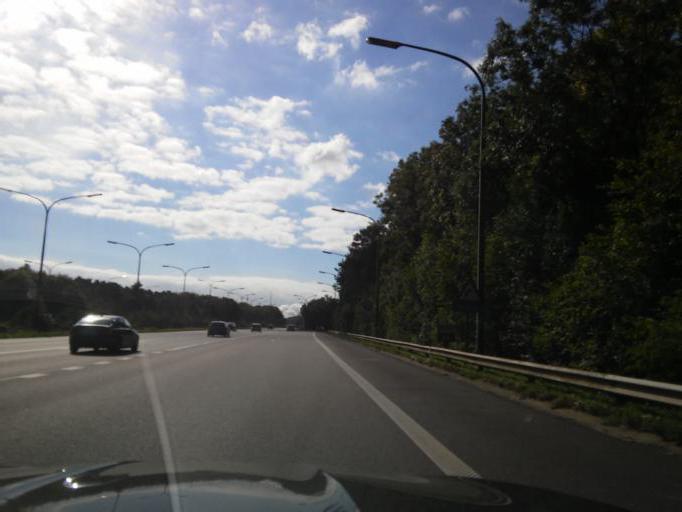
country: BE
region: Flanders
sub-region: Provincie Vlaams-Brabant
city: Halle
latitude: 50.7268
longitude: 4.2693
